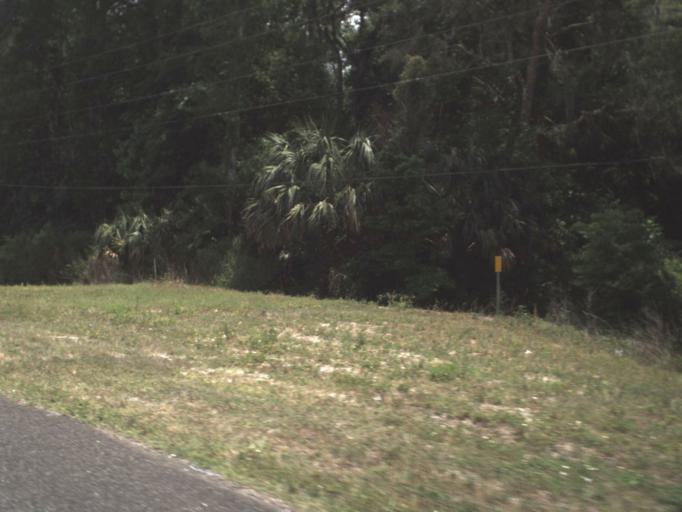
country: US
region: Florida
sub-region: Sumter County
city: Lake Panasoffkee
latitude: 28.8575
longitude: -82.1870
